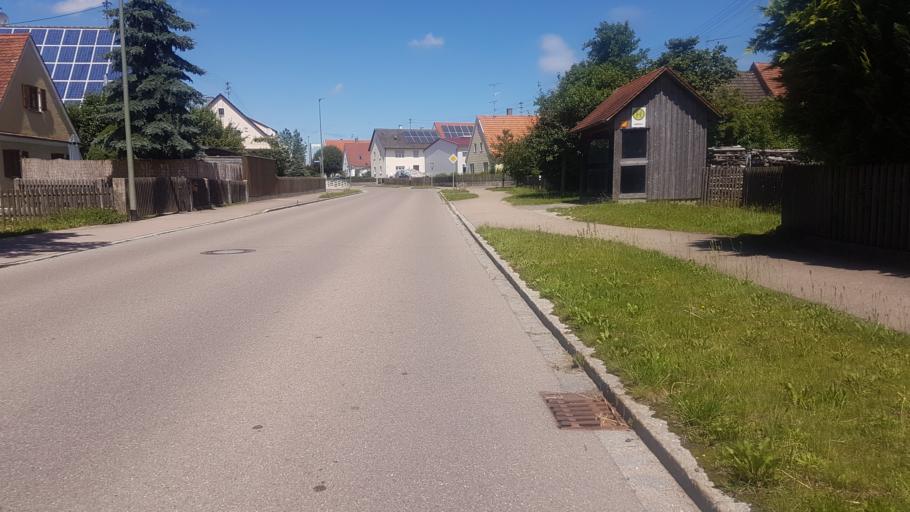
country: DE
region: Bavaria
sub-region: Swabia
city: Blindheim
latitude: 48.6325
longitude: 10.6187
